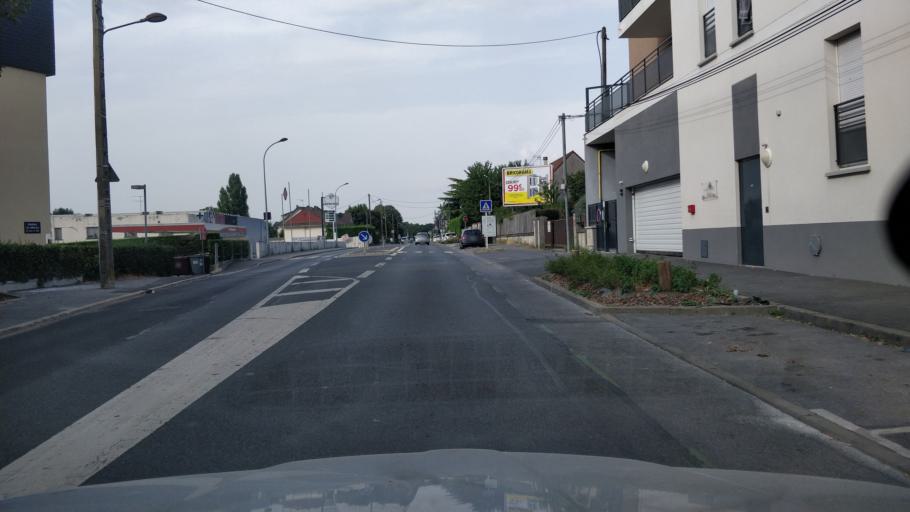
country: FR
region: Ile-de-France
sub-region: Departement de Seine-et-Marne
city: Thorigny-sur-Marne
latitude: 48.8943
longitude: 2.7093
